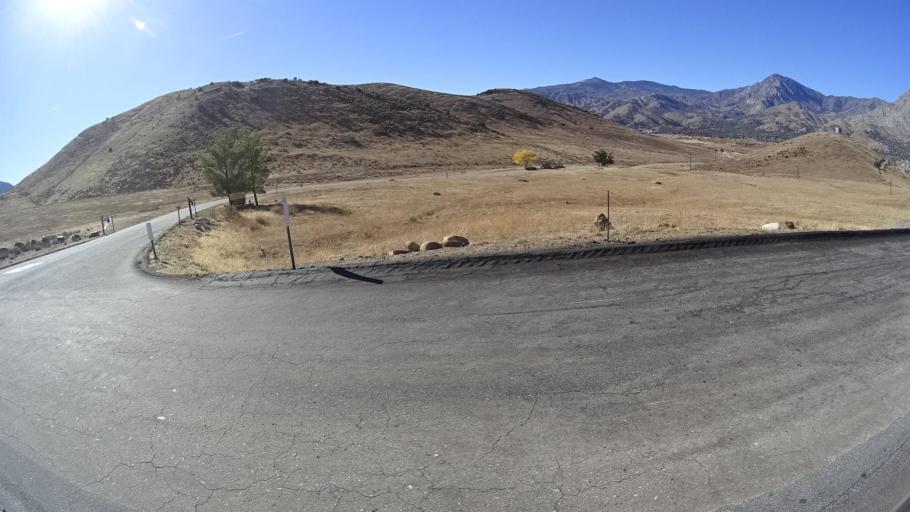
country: US
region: California
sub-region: Kern County
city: Wofford Heights
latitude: 35.6915
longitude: -118.4255
